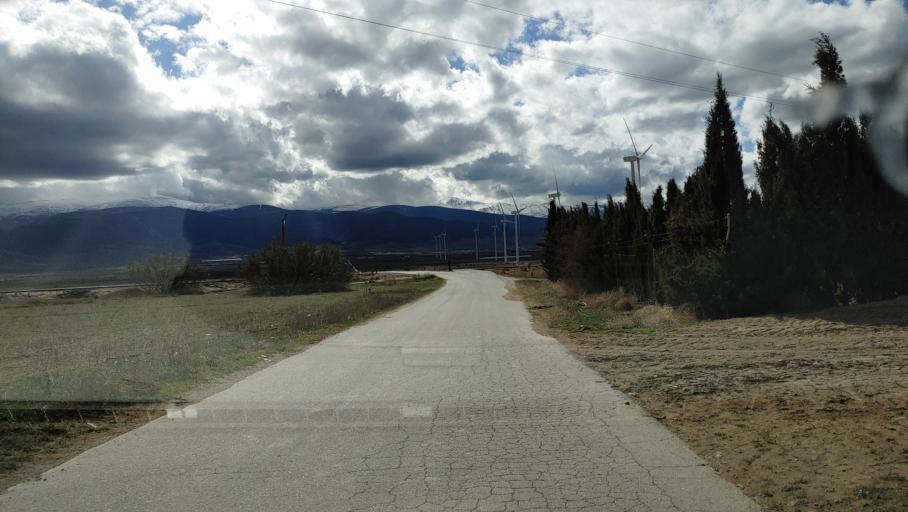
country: ES
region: Andalusia
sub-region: Provincia de Granada
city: Hueneja
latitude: 37.2213
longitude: -2.9680
